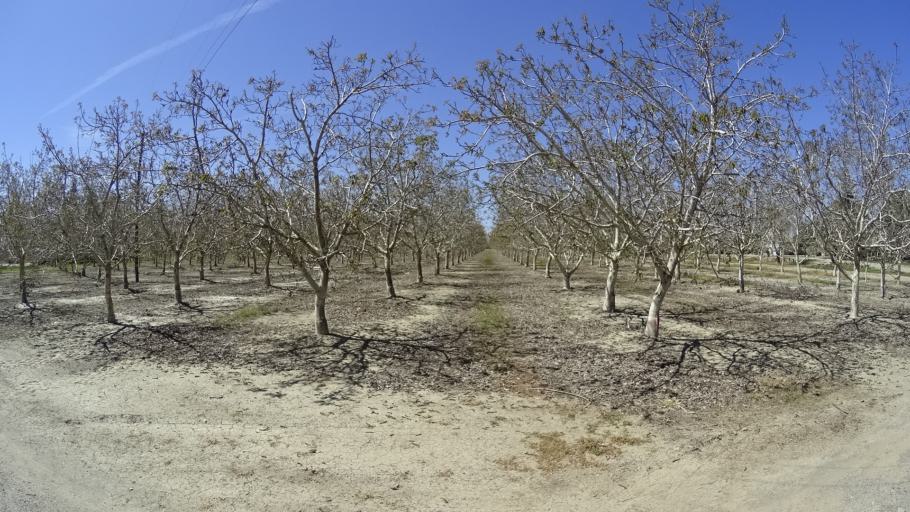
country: US
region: California
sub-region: Glenn County
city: Orland
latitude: 39.7210
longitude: -122.1091
